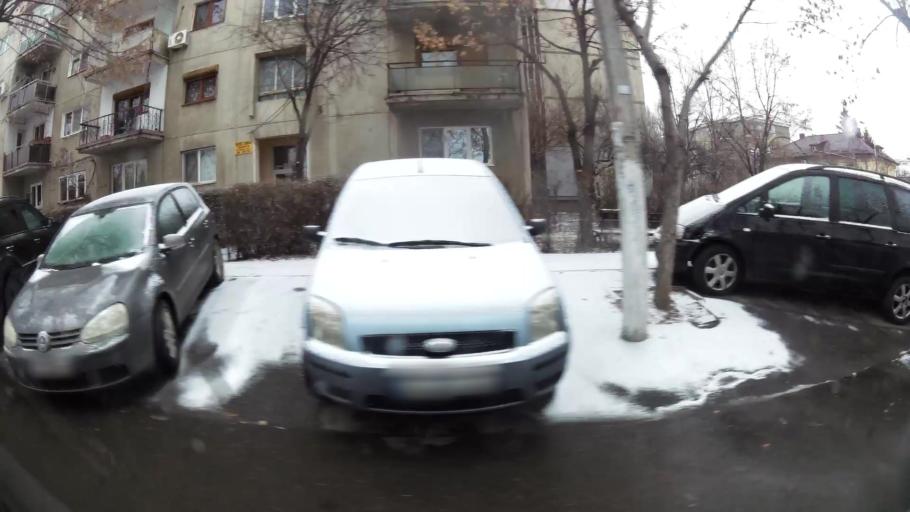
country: RO
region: Prahova
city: Ploiesti
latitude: 44.9387
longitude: 26.0033
